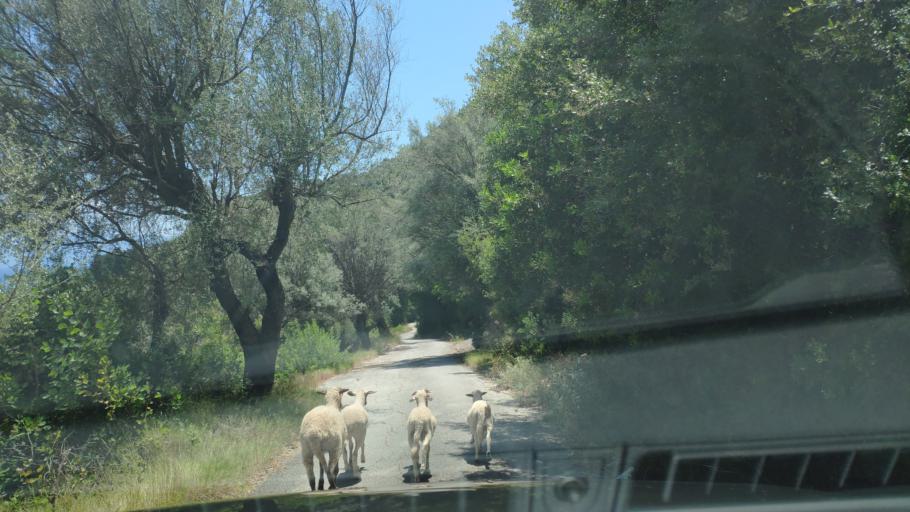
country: GR
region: Ionian Islands
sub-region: Lefkada
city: Nidri
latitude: 38.7535
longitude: 20.7138
